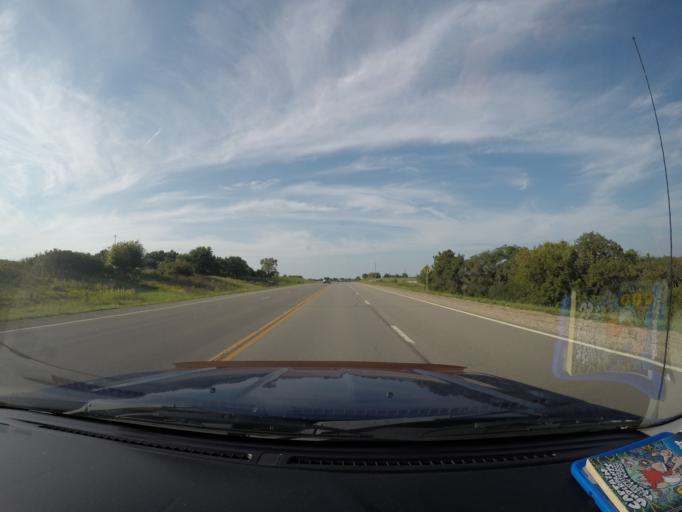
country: US
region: Kansas
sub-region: Atchison County
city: Atchison
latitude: 39.5295
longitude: -95.1329
